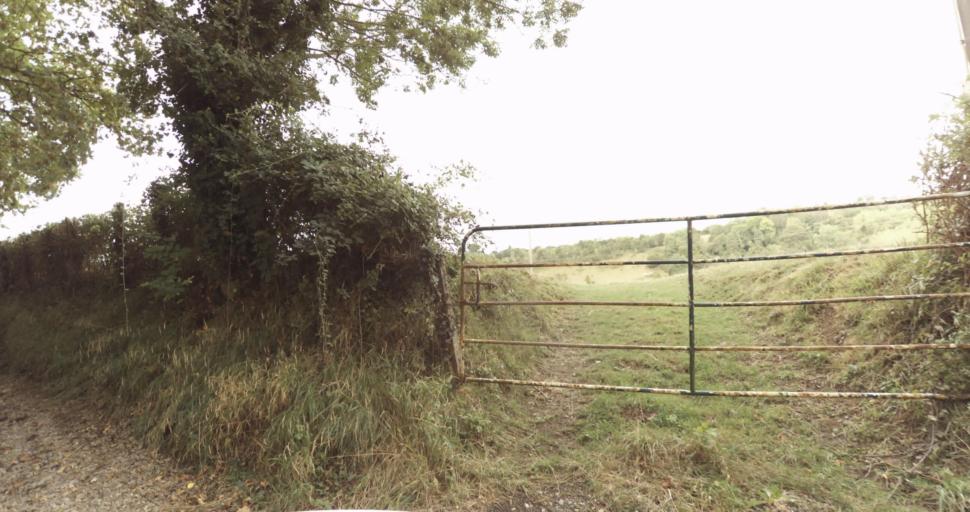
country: FR
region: Lower Normandy
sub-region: Departement de l'Orne
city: Vimoutiers
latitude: 48.9349
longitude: 0.1845
